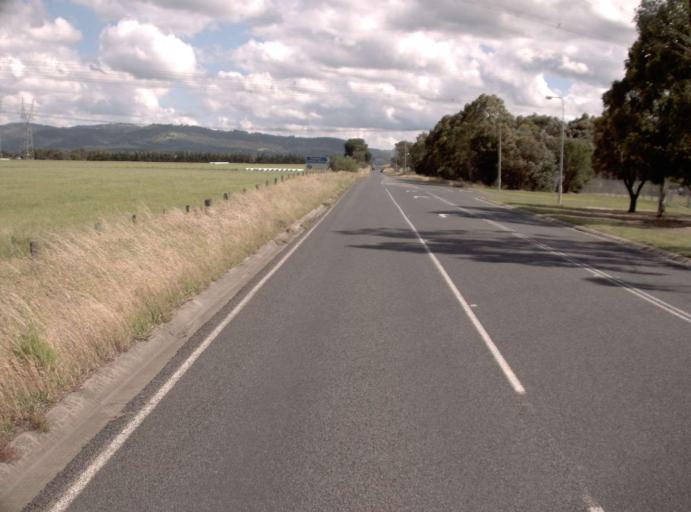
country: AU
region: Victoria
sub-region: Latrobe
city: Morwell
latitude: -38.2792
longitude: 146.4319
